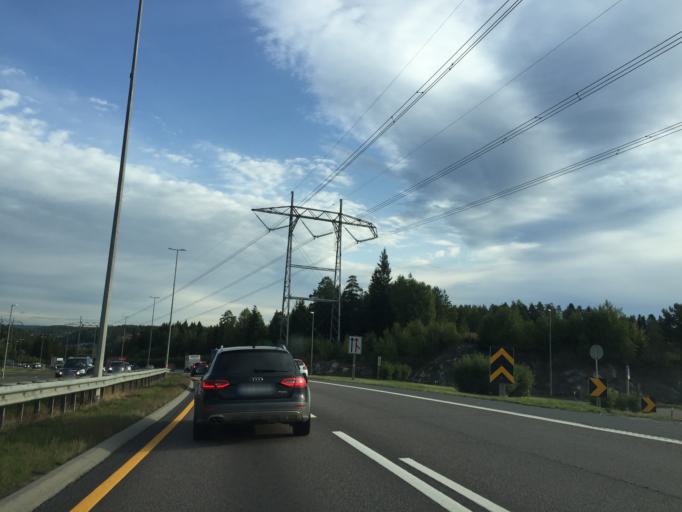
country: NO
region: Akershus
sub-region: Oppegard
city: Kolbotn
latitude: 59.8183
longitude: 10.8466
